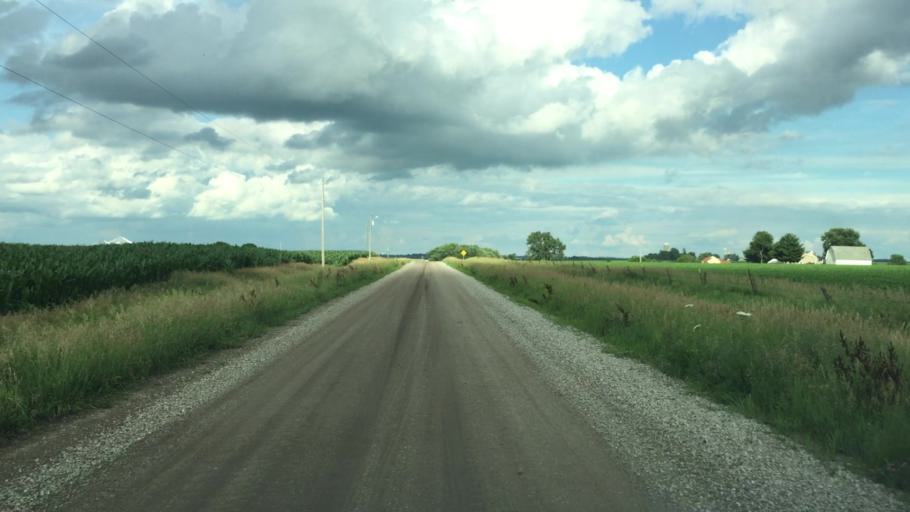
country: US
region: Iowa
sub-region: Jasper County
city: Monroe
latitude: 41.5663
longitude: -93.1020
